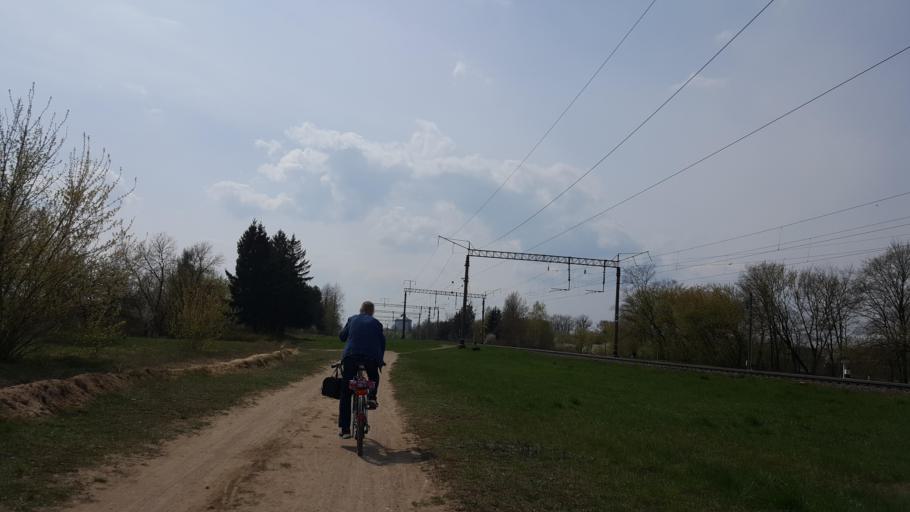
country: BY
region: Brest
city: Zhabinka
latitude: 52.1927
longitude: 23.9964
